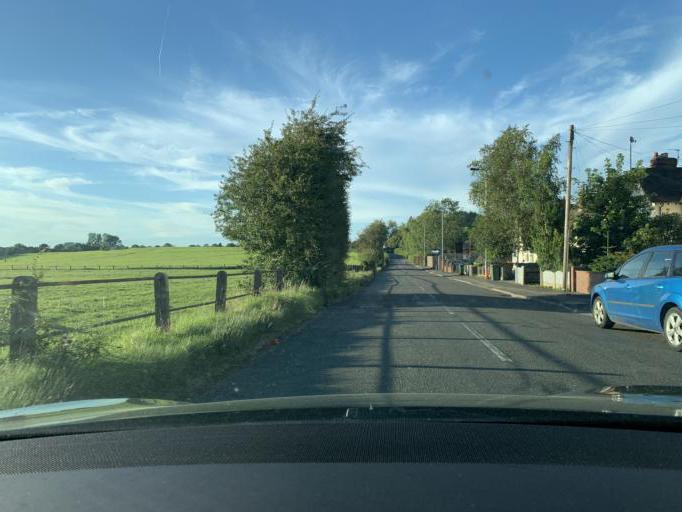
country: GB
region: England
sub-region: Staffordshire
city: Stafford
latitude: 52.8268
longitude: -2.1170
